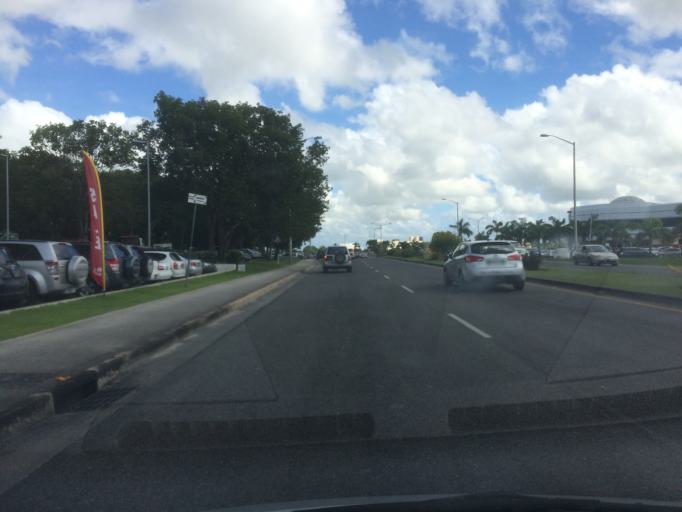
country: BB
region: Saint Michael
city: Bridgetown
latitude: 13.1425
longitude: -59.6080
